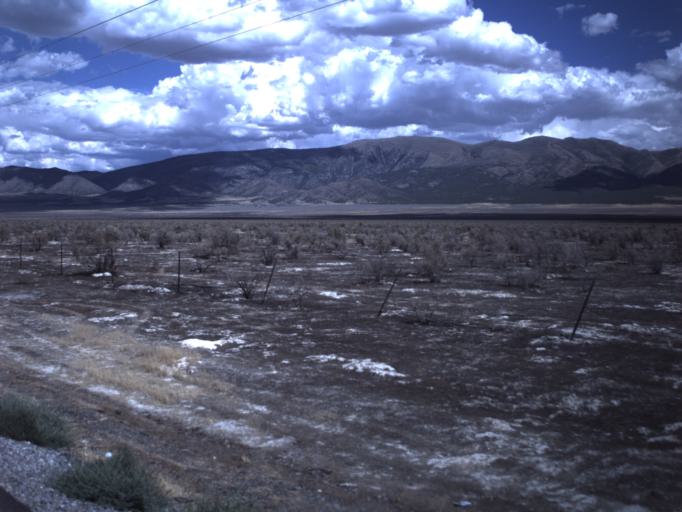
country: US
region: Utah
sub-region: Tooele County
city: Grantsville
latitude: 40.2491
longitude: -112.7047
